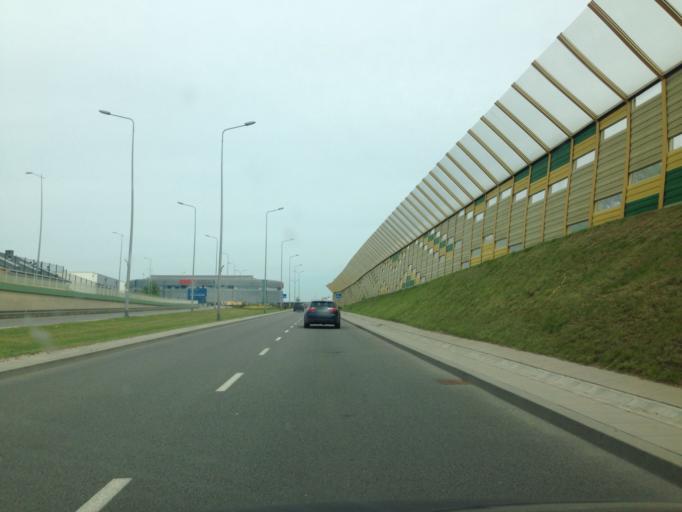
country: PL
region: Pomeranian Voivodeship
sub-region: Sopot
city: Sopot
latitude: 54.4240
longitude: 18.5737
